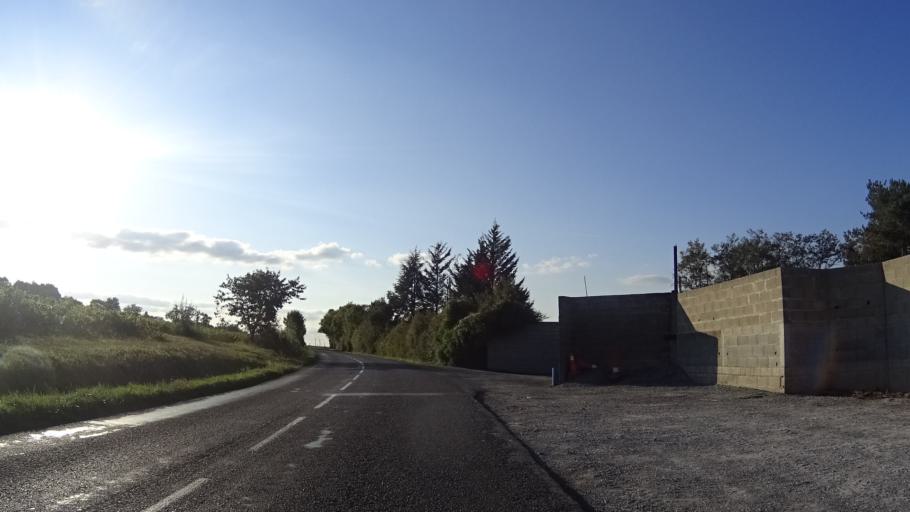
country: FR
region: Pays de la Loire
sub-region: Departement de Maine-et-Loire
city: Lire
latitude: 47.3420
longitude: -1.1455
